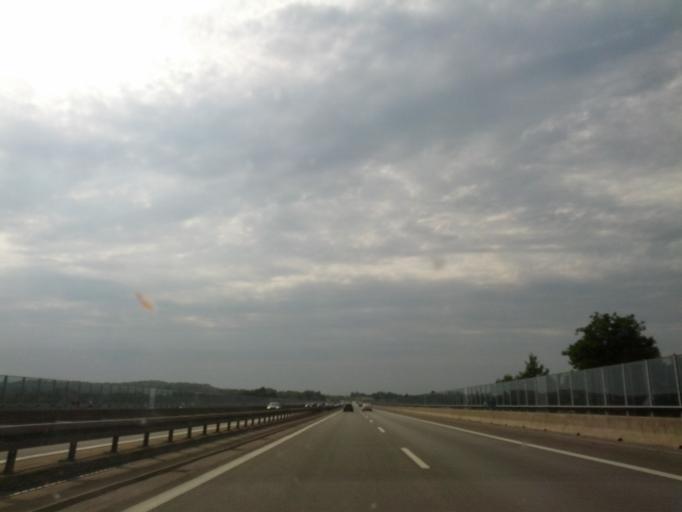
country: DE
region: Mecklenburg-Vorpommern
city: Papendorf
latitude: 54.0200
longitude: 12.1399
